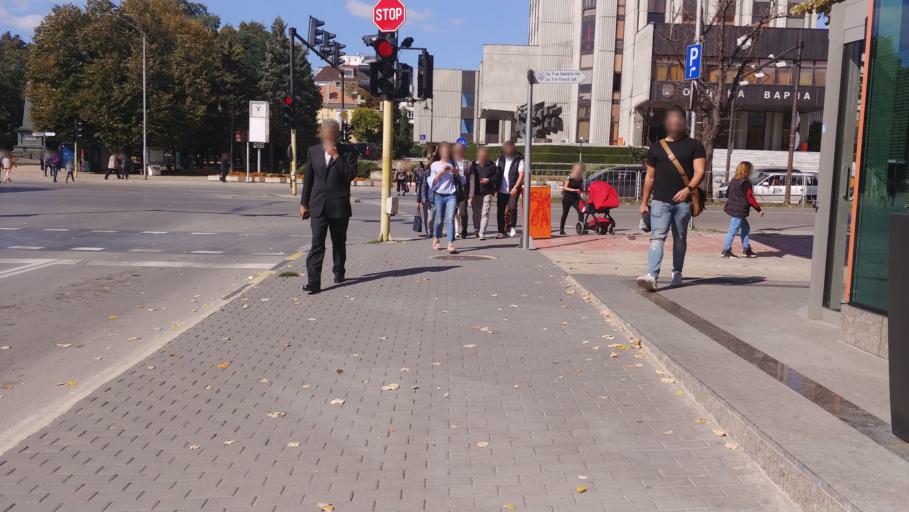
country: BG
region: Varna
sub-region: Obshtina Varna
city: Varna
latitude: 43.2072
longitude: 27.9181
